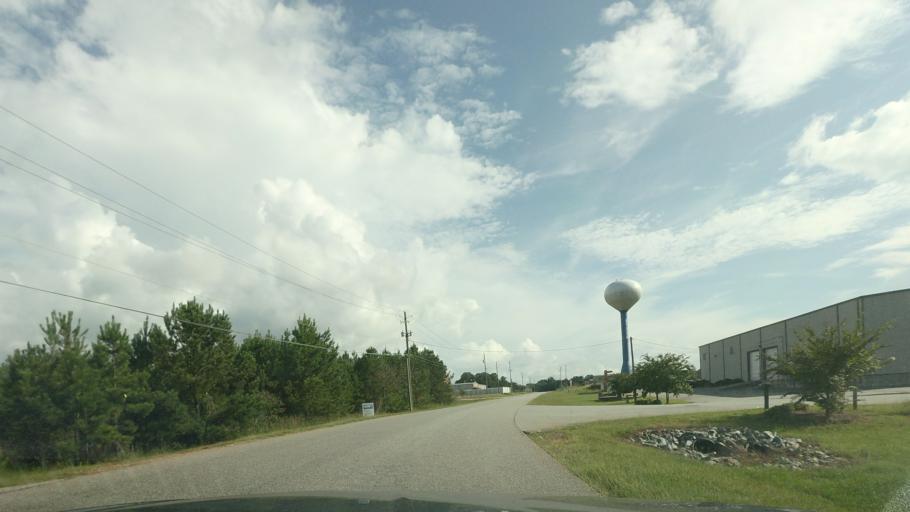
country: US
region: Georgia
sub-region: Peach County
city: Byron
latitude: 32.6487
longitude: -83.7408
